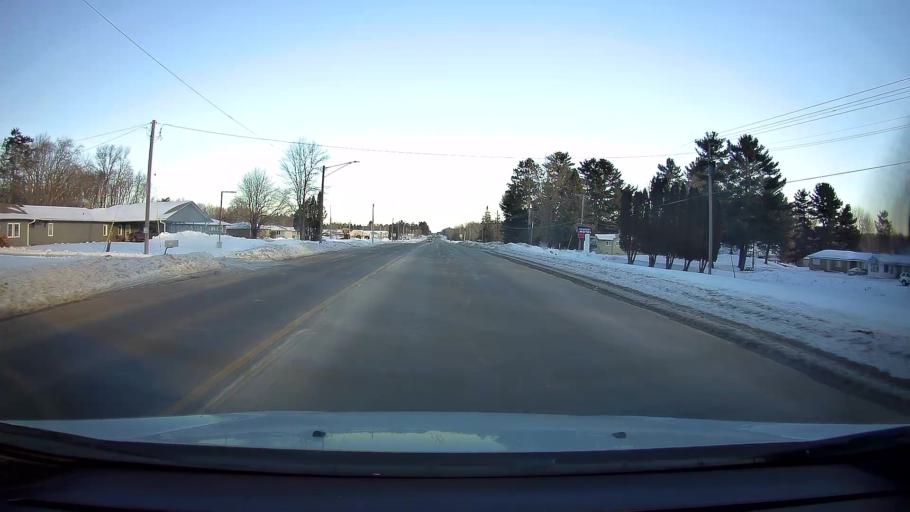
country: US
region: Wisconsin
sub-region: Barron County
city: Cumberland
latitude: 45.5484
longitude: -92.0171
